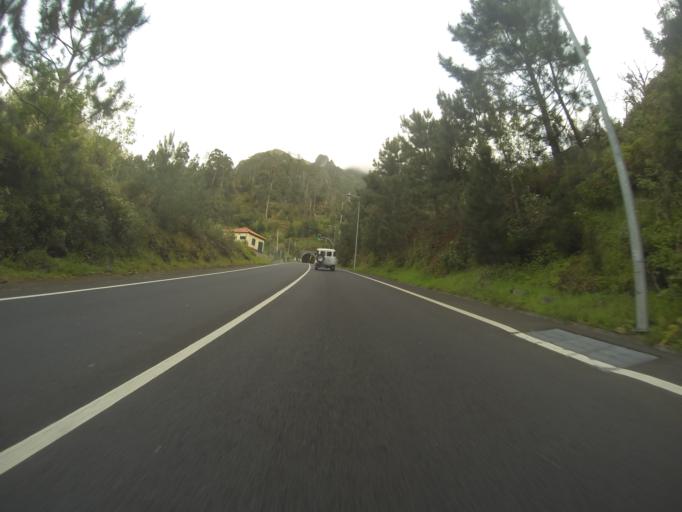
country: PT
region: Madeira
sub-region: Sao Vicente
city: Sao Vicente
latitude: 32.7682
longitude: -17.0303
